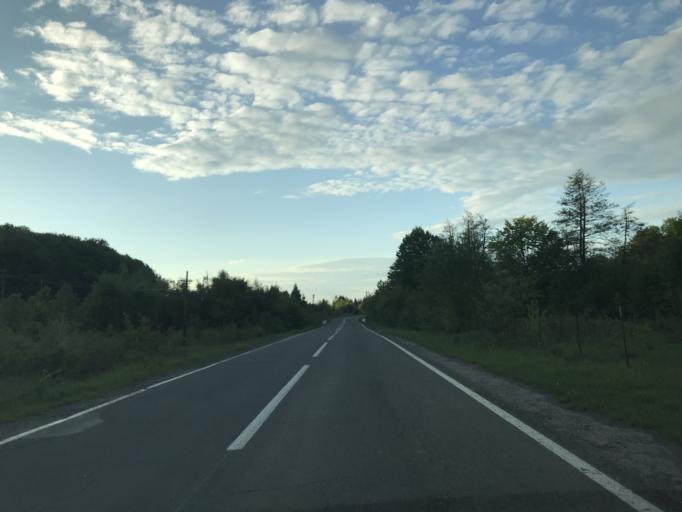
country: RO
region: Sibiu
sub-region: Comuna Cartisoara
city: Cartisoara
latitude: 45.6906
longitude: 24.5735
